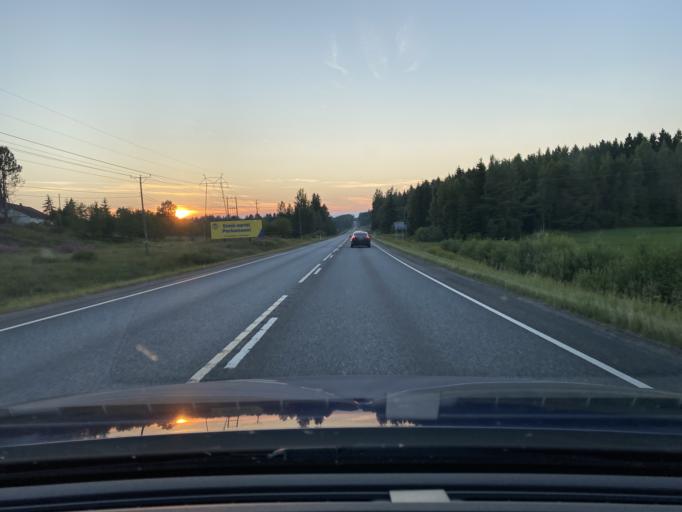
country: FI
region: Pirkanmaa
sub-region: Luoteis-Pirkanmaa
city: Ikaalinen
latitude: 61.8065
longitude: 22.9649
